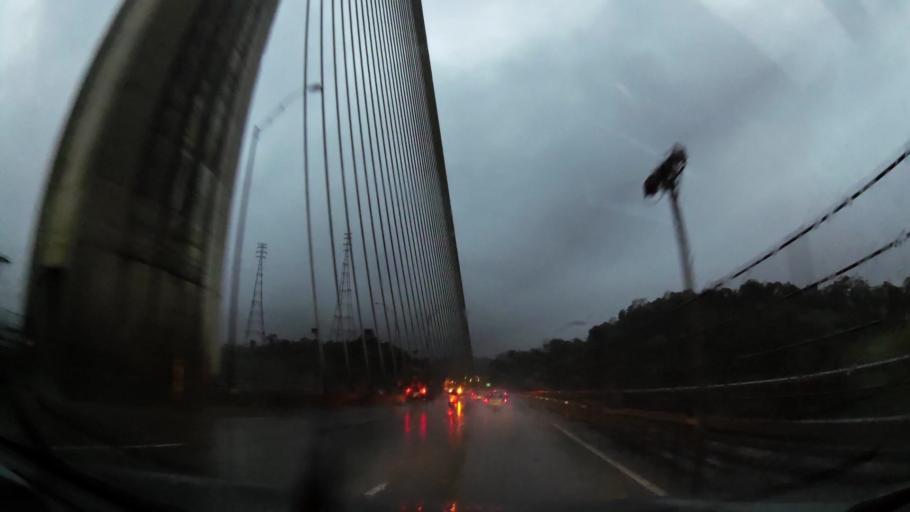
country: PA
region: Panama
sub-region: Distrito de Panama
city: Paraiso
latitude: 9.0301
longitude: -79.6363
